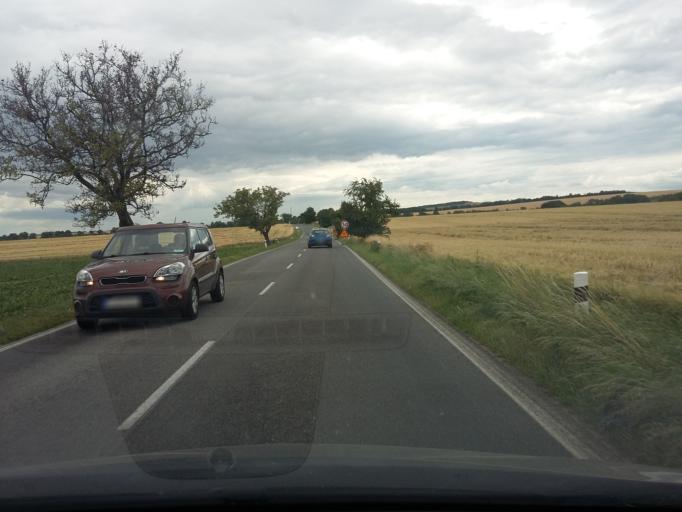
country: SK
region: Trnavsky
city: Vrbove
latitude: 48.5821
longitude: 17.6545
